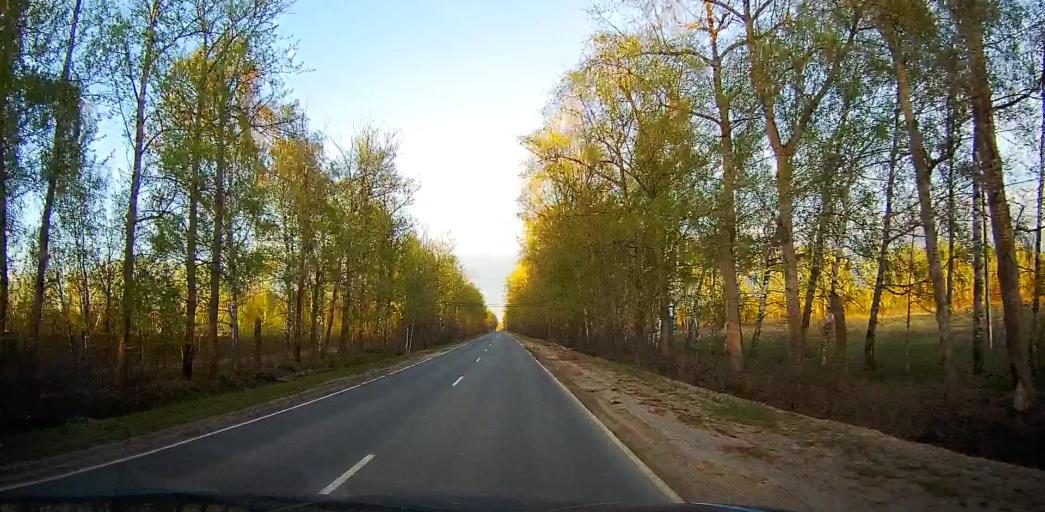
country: RU
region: Moskovskaya
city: Peski
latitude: 55.2090
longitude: 38.7160
